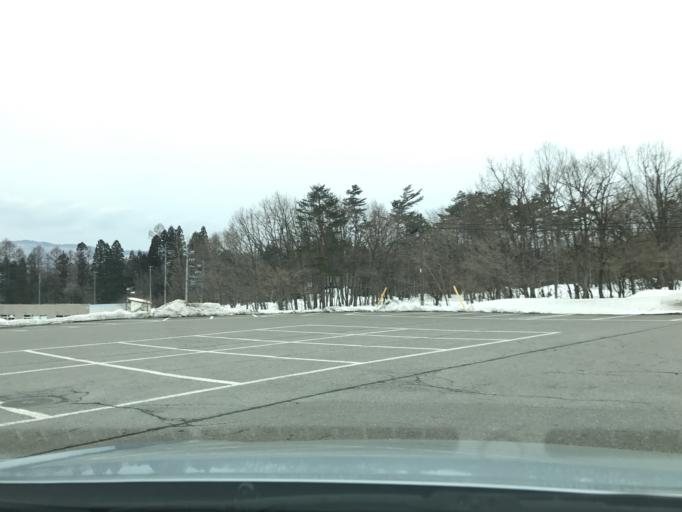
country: JP
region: Nagano
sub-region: Kitaazumi Gun
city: Hakuba
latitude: 36.6942
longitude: 137.8354
